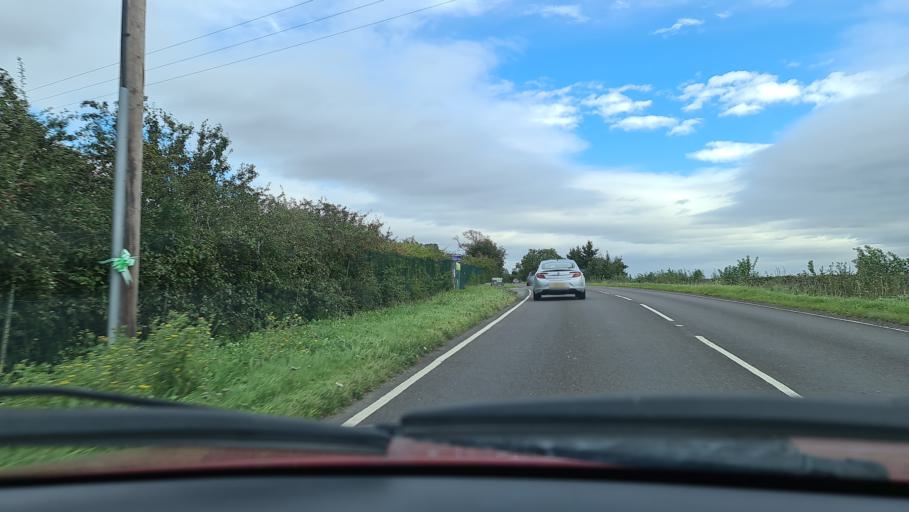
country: GB
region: England
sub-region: Oxfordshire
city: Somerton
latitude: 51.9749
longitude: -1.2325
